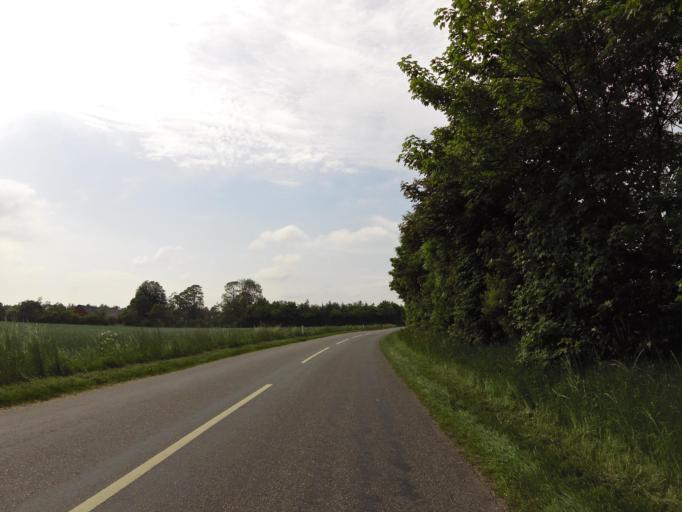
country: DK
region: South Denmark
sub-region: Haderslev Kommune
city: Gram
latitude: 55.2751
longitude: 9.1194
